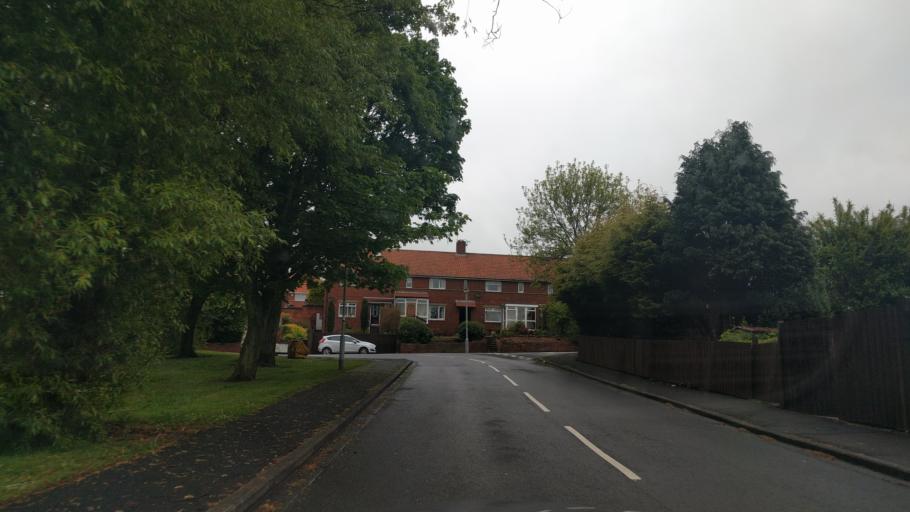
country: GB
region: England
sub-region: Northumberland
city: Morpeth
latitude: 55.1611
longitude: -1.6939
